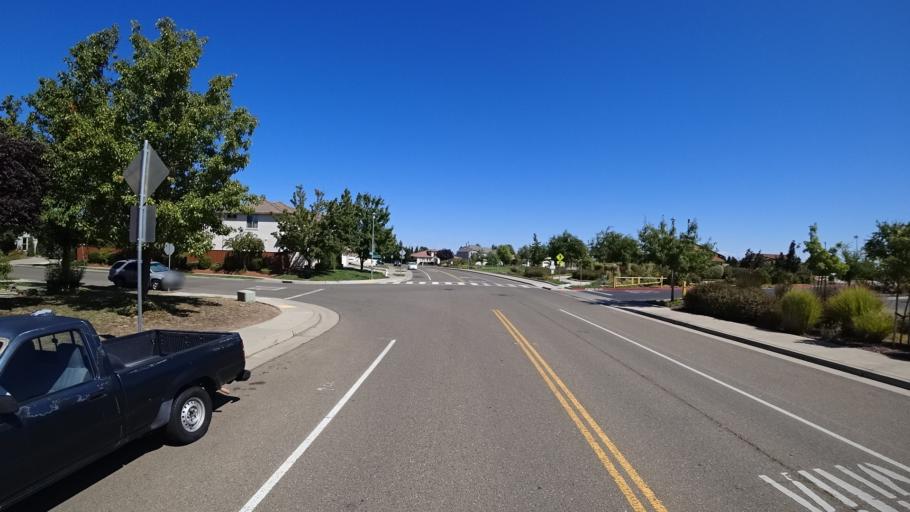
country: US
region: California
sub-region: Sacramento County
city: Elk Grove
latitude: 38.4028
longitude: -121.3403
